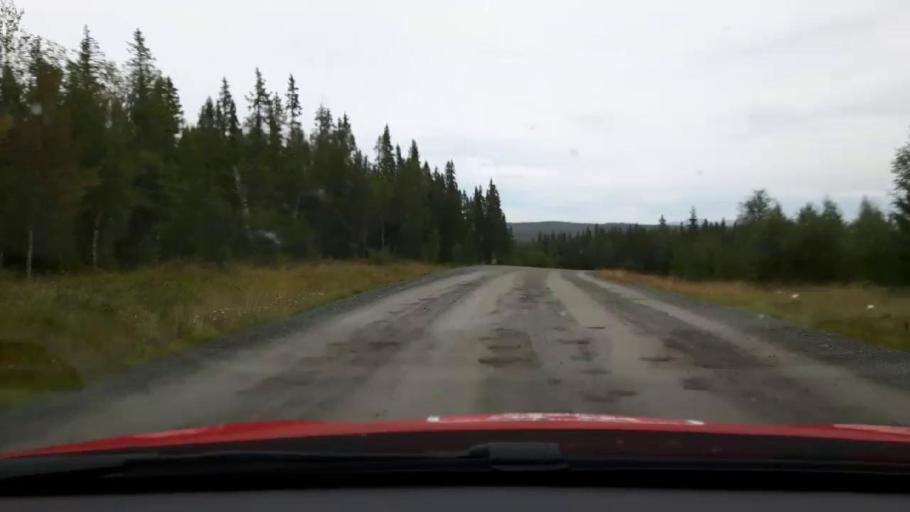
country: SE
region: Jaemtland
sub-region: Are Kommun
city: Are
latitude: 63.4698
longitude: 12.5807
